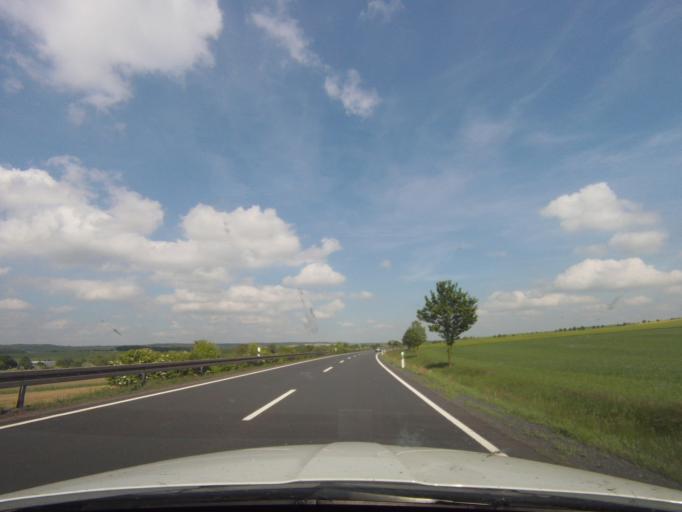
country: DE
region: Thuringia
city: Dreitzsch
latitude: 50.7363
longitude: 11.7788
